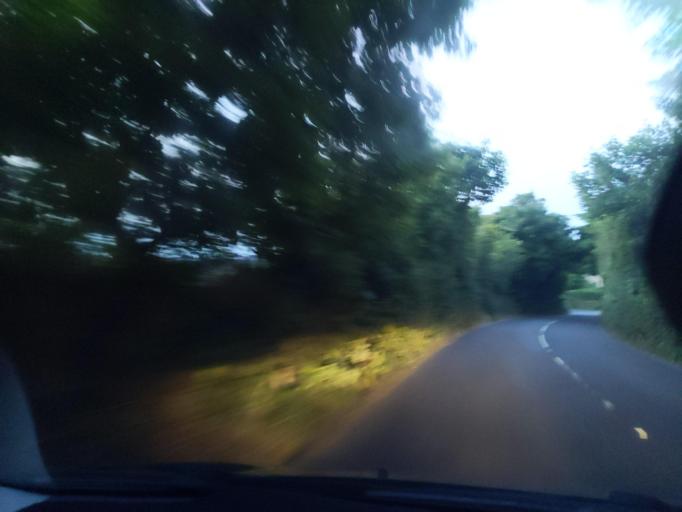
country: GB
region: England
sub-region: Cornwall
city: Camborne
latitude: 50.1869
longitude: -5.3103
